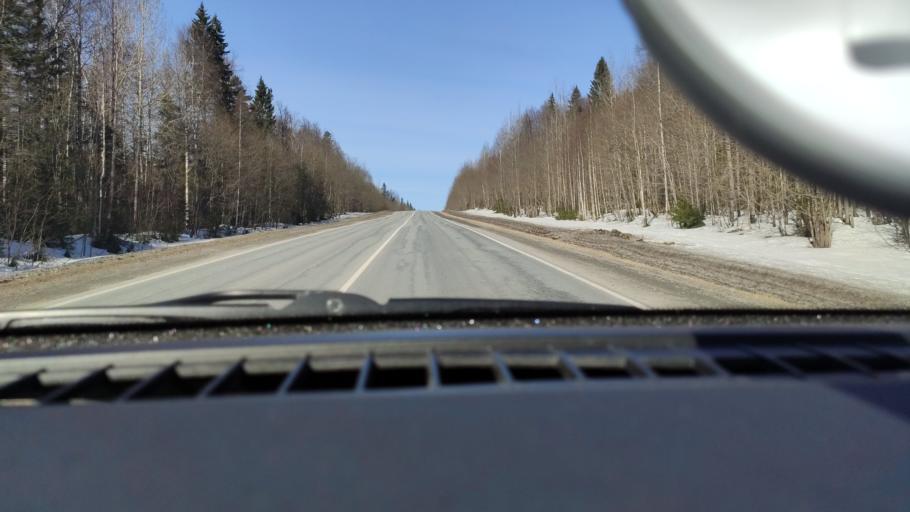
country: RU
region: Perm
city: Perm
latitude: 58.1665
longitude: 56.2393
